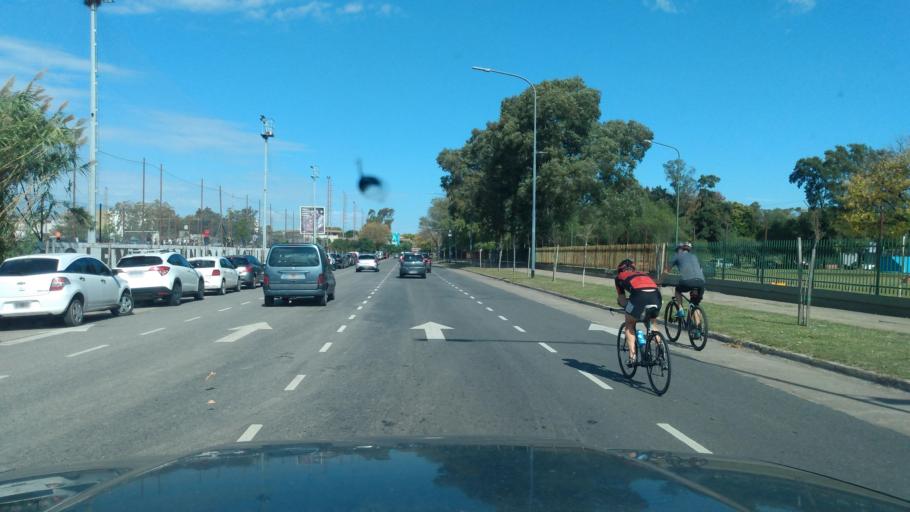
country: AR
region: Buenos Aires
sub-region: Partido de General San Martin
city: General San Martin
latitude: -34.5594
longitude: -58.4959
